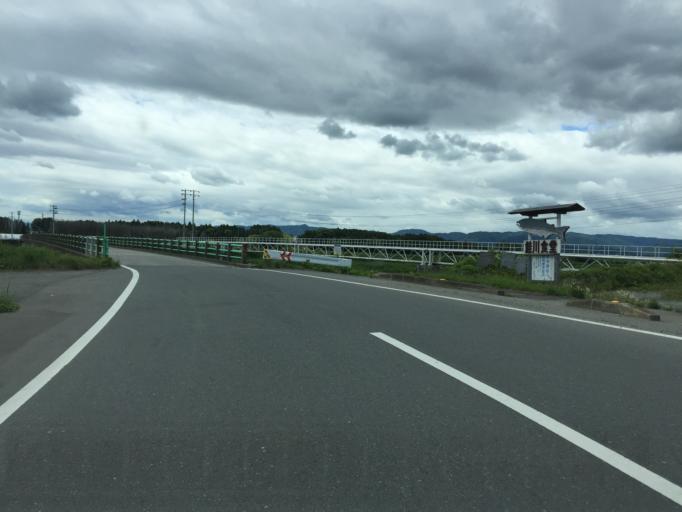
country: JP
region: Fukushima
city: Namie
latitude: 37.6450
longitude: 141.0027
